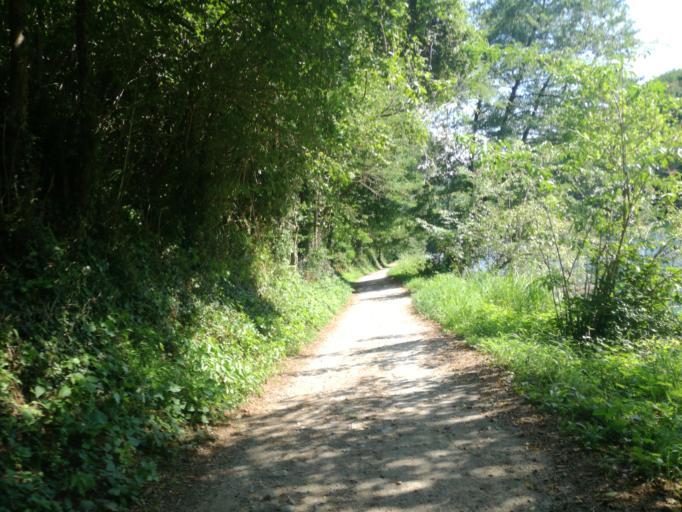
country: IT
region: Lombardy
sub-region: Provincia di Lecco
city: Imbersago
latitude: 45.6927
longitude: 9.4532
